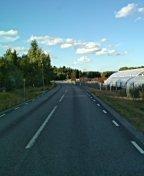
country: SE
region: Uppsala
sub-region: Habo Kommun
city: Balsta
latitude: 59.6331
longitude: 17.5147
